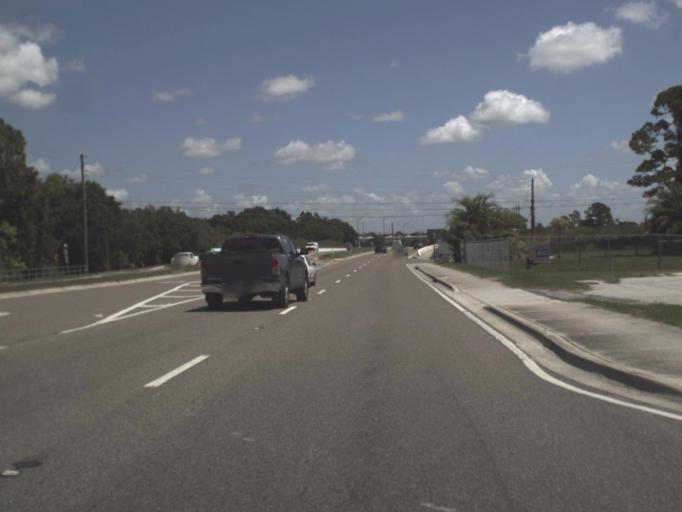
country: US
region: Florida
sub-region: Pinellas County
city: Oldsmar
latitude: 28.0348
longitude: -82.6830
